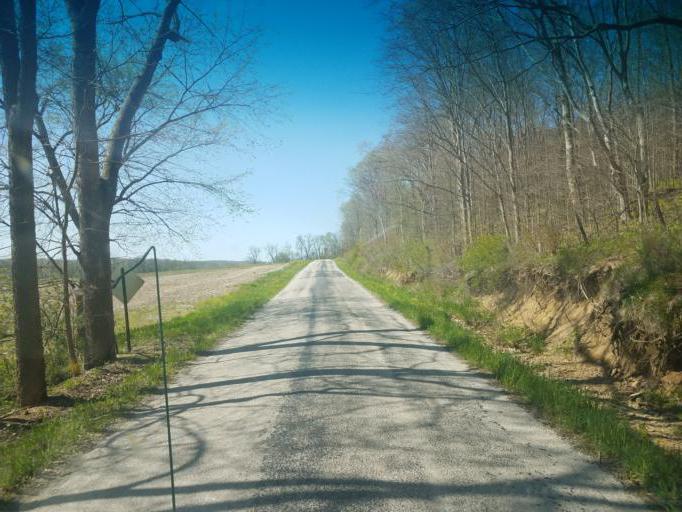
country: US
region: Ohio
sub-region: Medina County
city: Lodi
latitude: 40.9450
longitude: -82.0166
